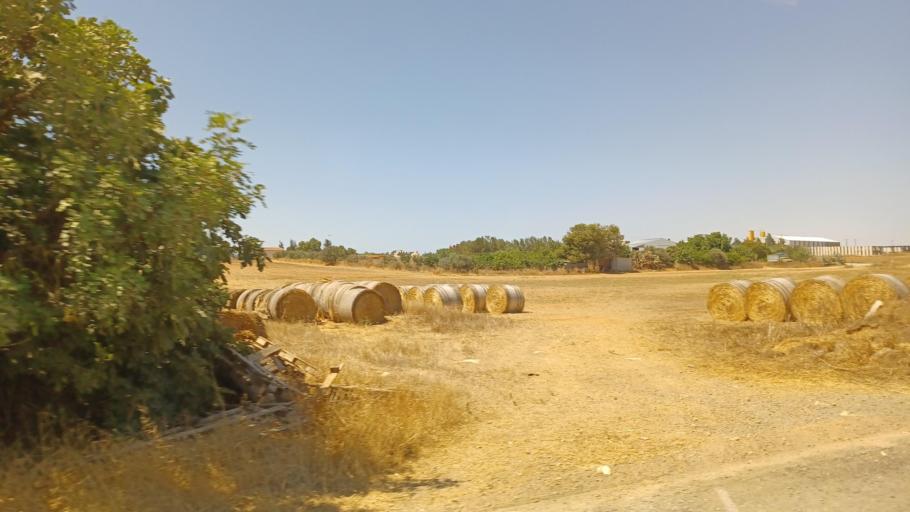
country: CY
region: Larnaka
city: Xylotymbou
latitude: 35.0122
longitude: 33.7300
